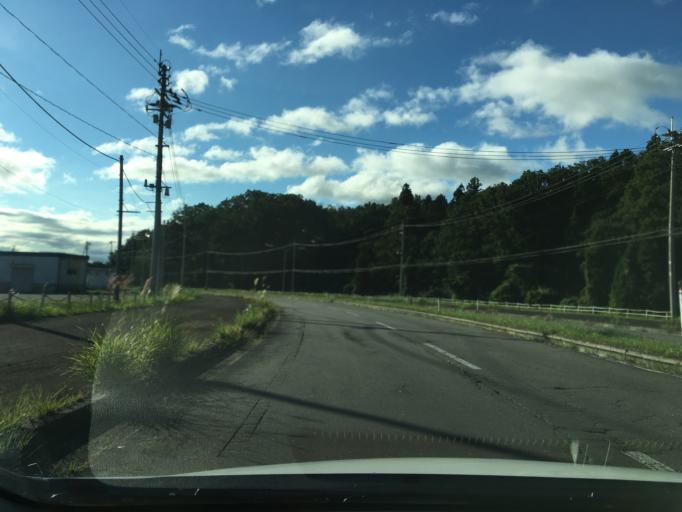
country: JP
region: Yamagata
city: Yonezawa
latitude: 37.9114
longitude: 140.1702
